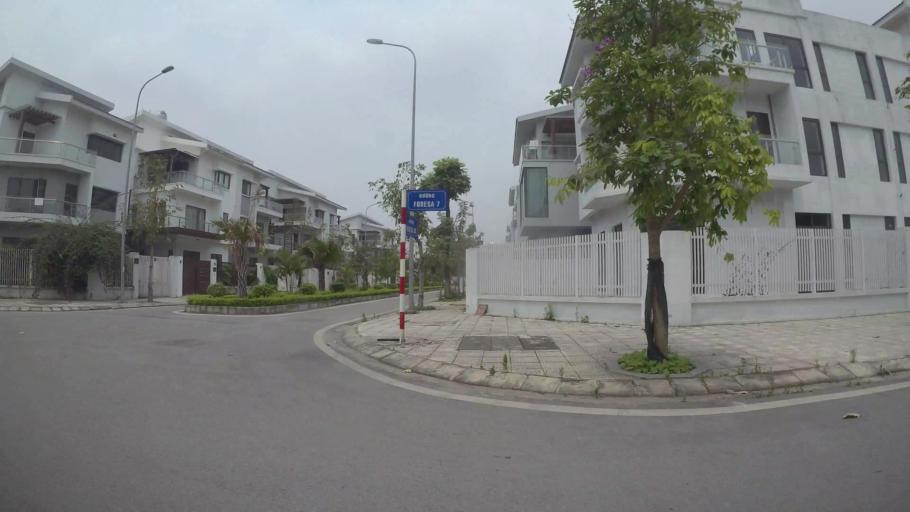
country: VN
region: Ha Noi
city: Cau Dien
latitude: 21.0277
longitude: 105.7461
